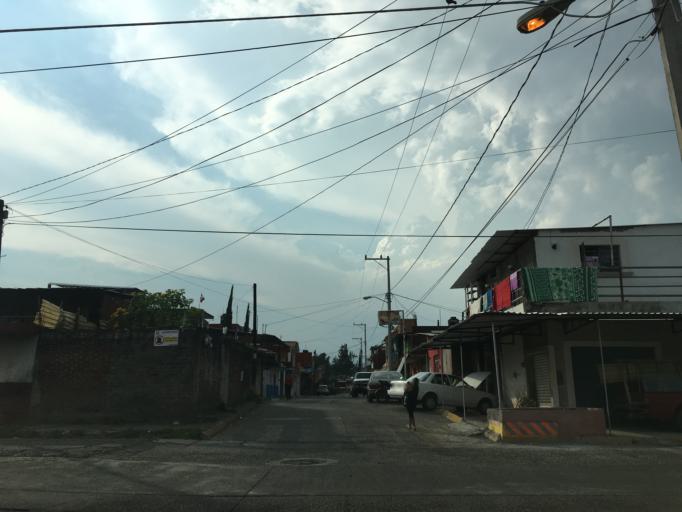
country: MX
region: Michoacan
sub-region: Uruapan
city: Uruapan
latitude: 19.4095
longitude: -102.0500
